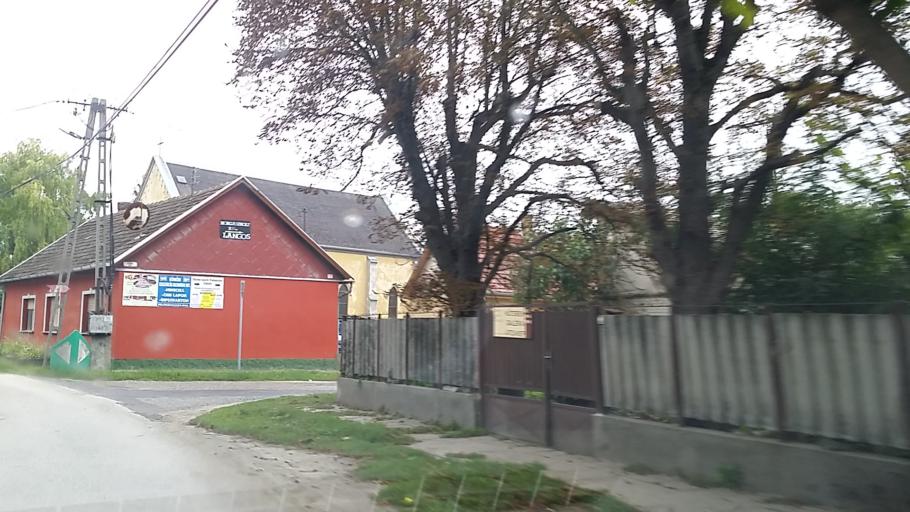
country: HU
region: Pest
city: Domsod
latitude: 47.0942
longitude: 19.0030
